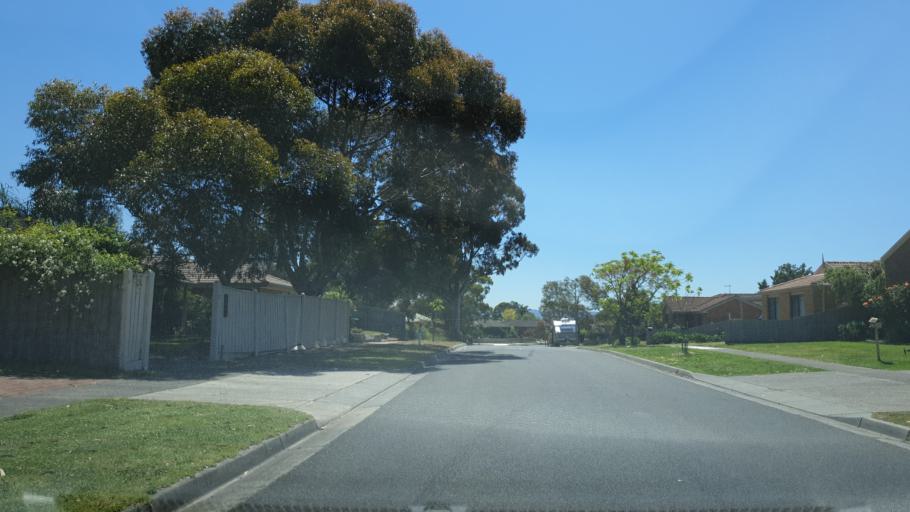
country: AU
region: Victoria
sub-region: Casey
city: Cranbourne North
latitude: -38.0800
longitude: 145.2912
